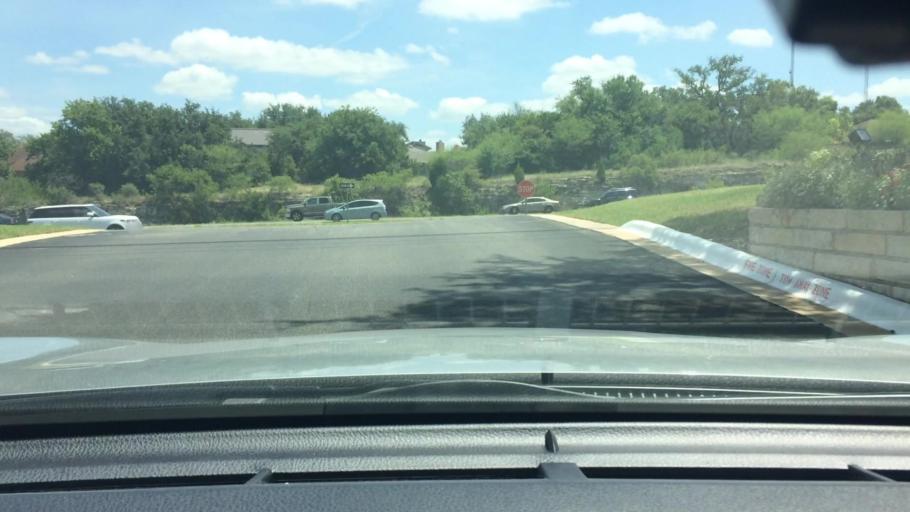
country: US
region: Texas
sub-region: Travis County
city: West Lake Hills
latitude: 30.3344
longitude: -97.8076
